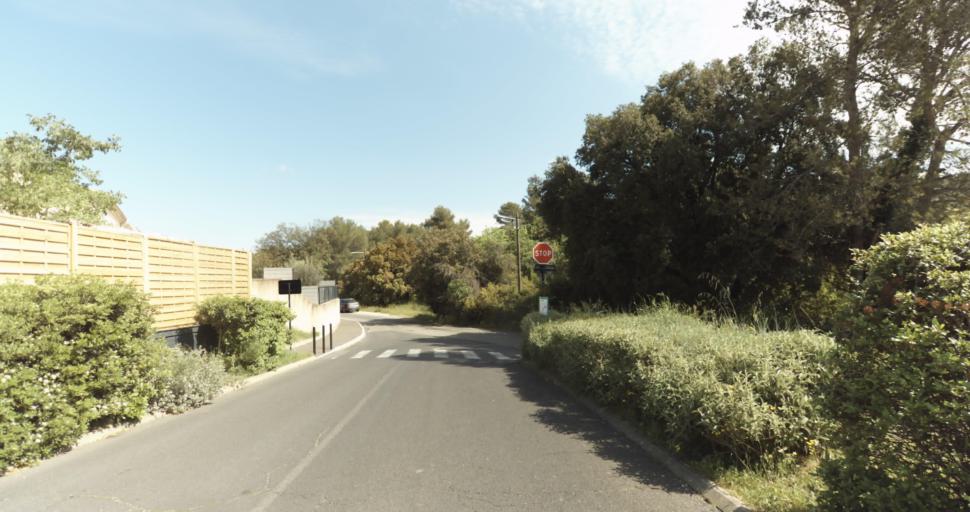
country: FR
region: Languedoc-Roussillon
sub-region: Departement du Gard
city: Nimes
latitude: 43.8508
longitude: 4.3159
